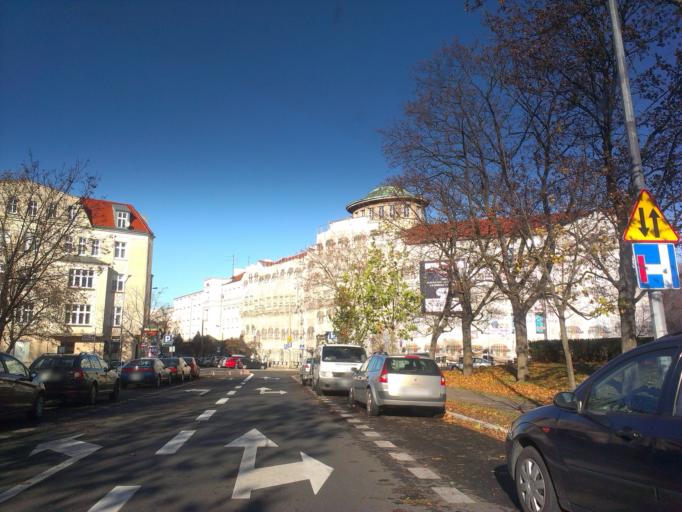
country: PL
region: Greater Poland Voivodeship
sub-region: Poznan
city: Poznan
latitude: 52.4033
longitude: 16.9429
